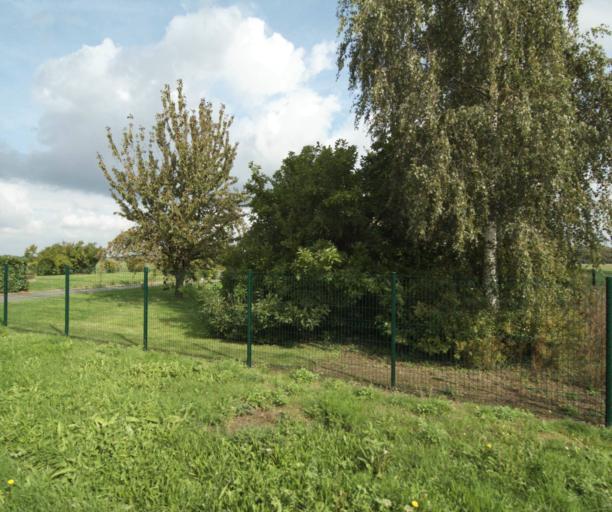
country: FR
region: Nord-Pas-de-Calais
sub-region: Departement du Nord
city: Perenchies
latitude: 50.6784
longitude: 2.9510
